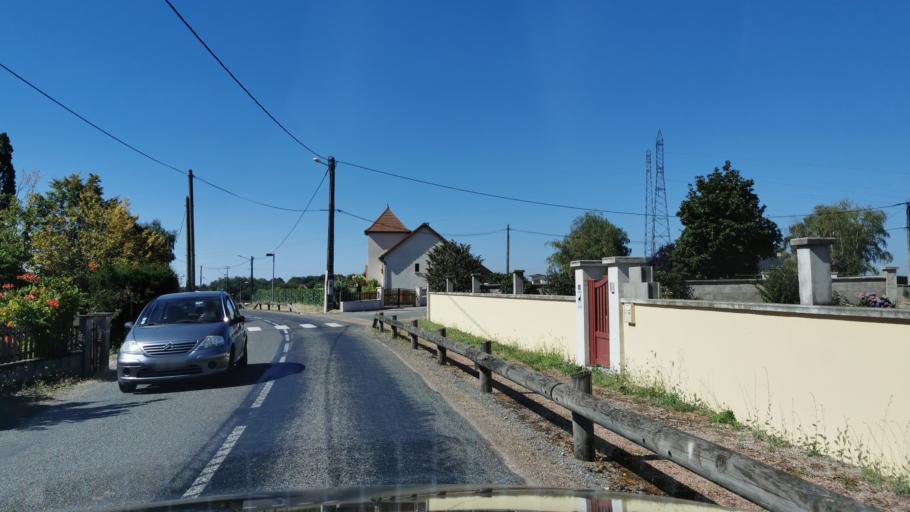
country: FR
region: Bourgogne
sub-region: Departement de Saone-et-Loire
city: Torcy
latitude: 46.7808
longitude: 4.4770
